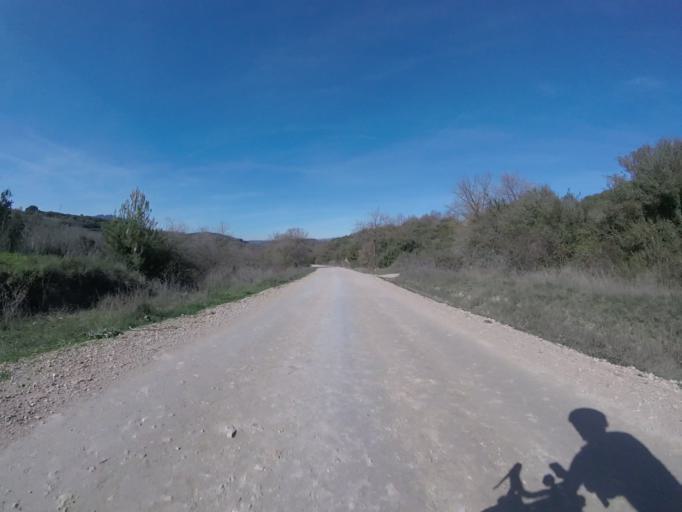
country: ES
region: Navarre
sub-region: Provincia de Navarra
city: Oteiza
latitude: 42.6456
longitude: -1.9614
